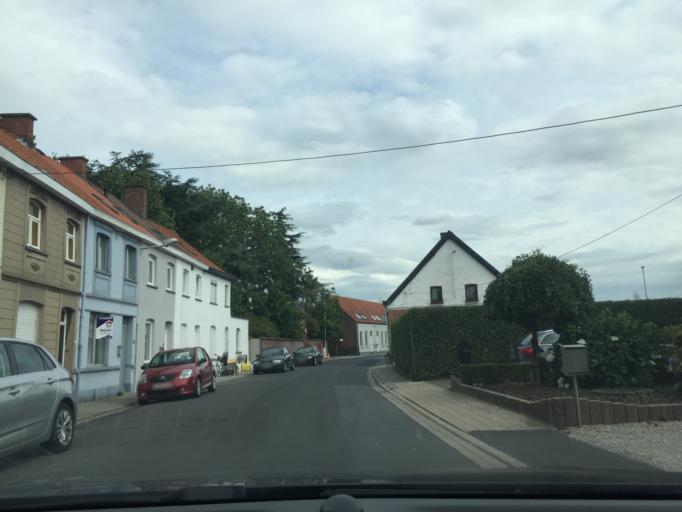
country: BE
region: Flanders
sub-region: Provincie West-Vlaanderen
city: Izegem
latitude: 50.9155
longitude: 3.2253
